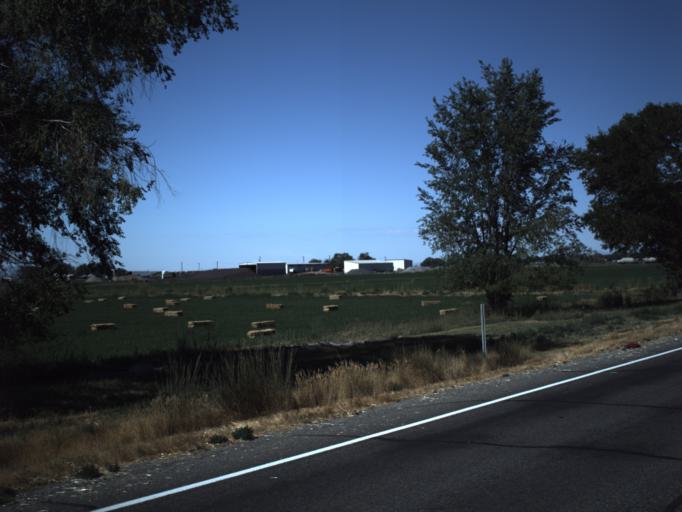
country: US
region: Utah
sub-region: Millard County
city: Delta
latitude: 39.3307
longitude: -112.6468
